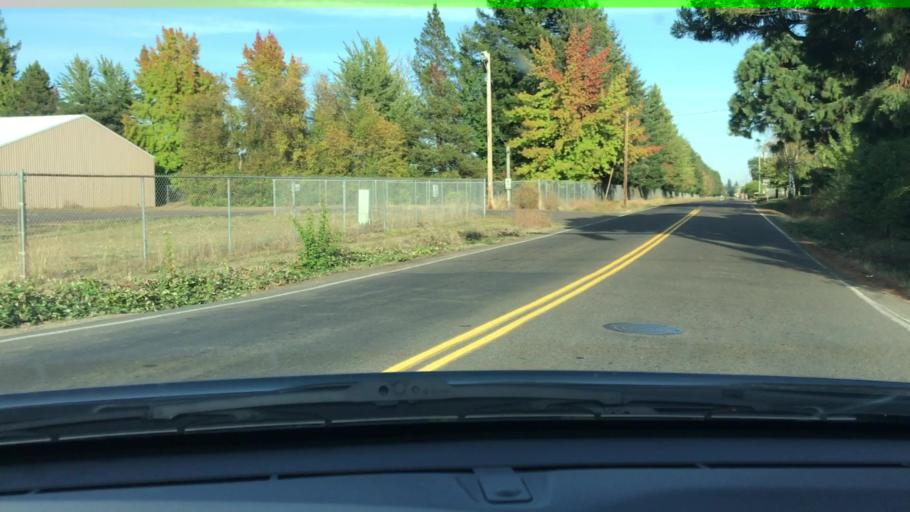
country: US
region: Oregon
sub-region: Yamhill County
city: McMinnville
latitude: 45.1929
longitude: -123.2098
